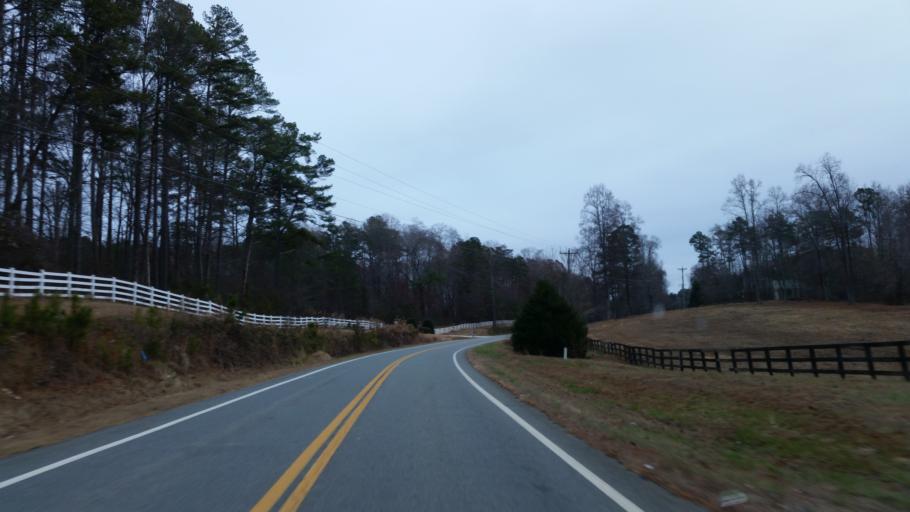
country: US
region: Georgia
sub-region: Dawson County
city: Dawsonville
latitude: 34.4440
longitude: -84.1003
